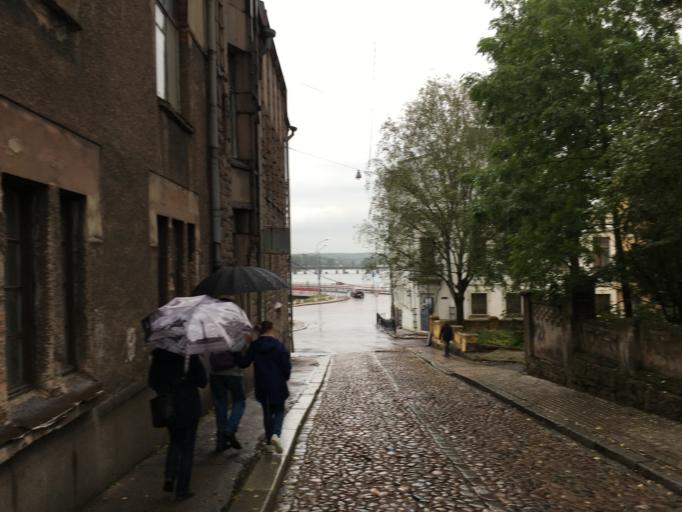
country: RU
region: Leningrad
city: Vyborg
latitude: 60.7145
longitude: 28.7323
